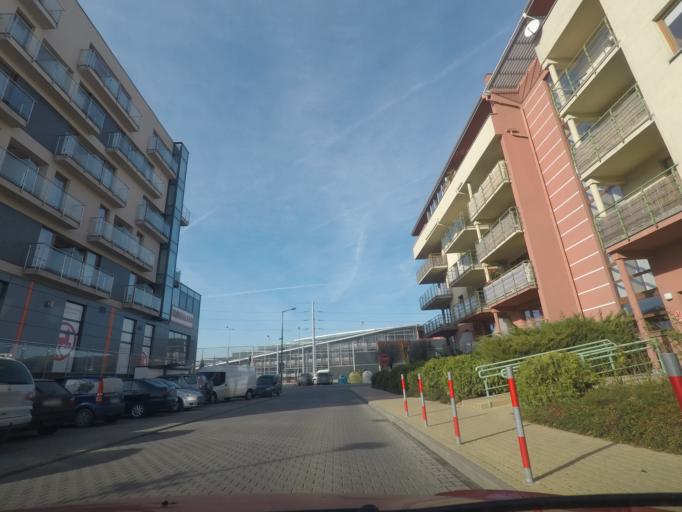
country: PL
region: Lesser Poland Voivodeship
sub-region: Krakow
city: Sidzina
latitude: 50.0208
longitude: 19.8998
